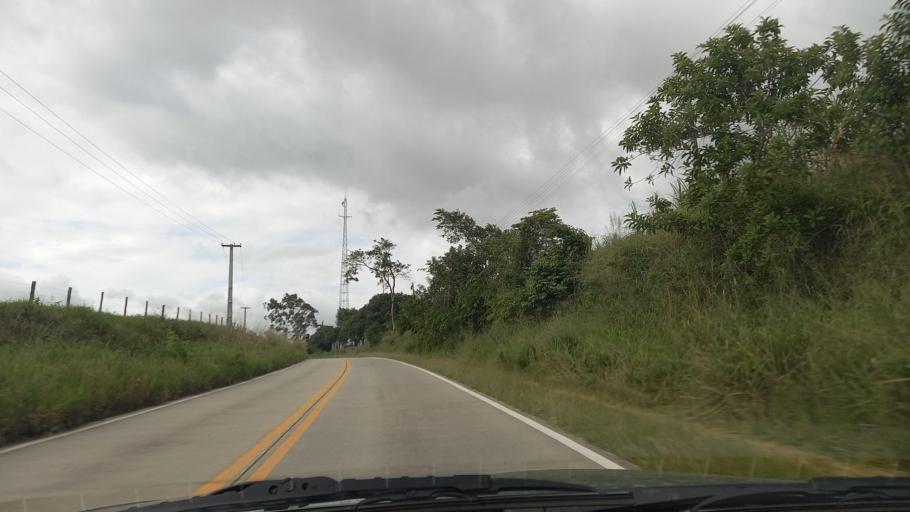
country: BR
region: Pernambuco
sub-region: Quipapa
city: Quipapa
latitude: -8.7969
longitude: -35.9956
